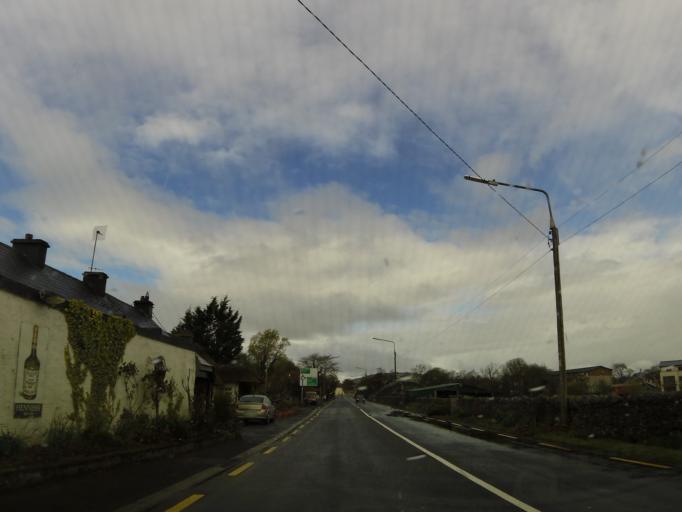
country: IE
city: Ballisodare
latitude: 54.2072
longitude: -8.5062
